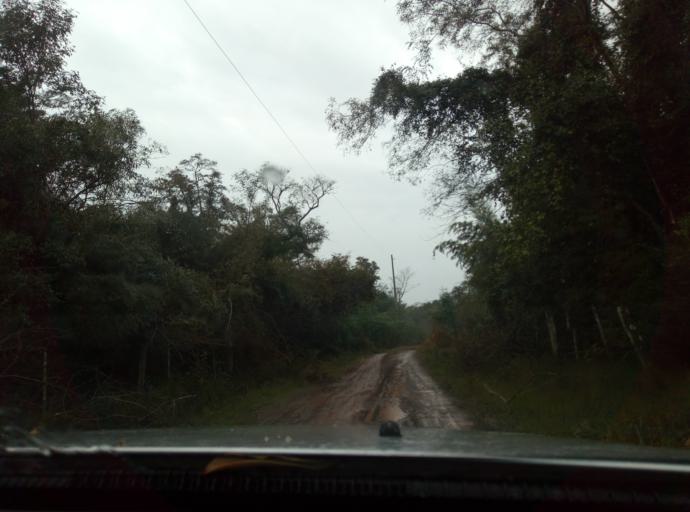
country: PY
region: Caaguazu
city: Carayao
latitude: -25.1063
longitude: -56.4140
